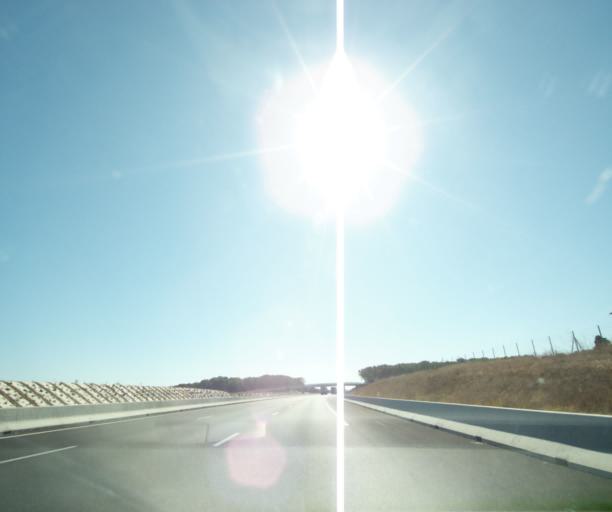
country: FR
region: Languedoc-Roussillon
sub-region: Departement de l'Herault
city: Saint-Aunes
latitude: 43.6103
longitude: 3.9469
